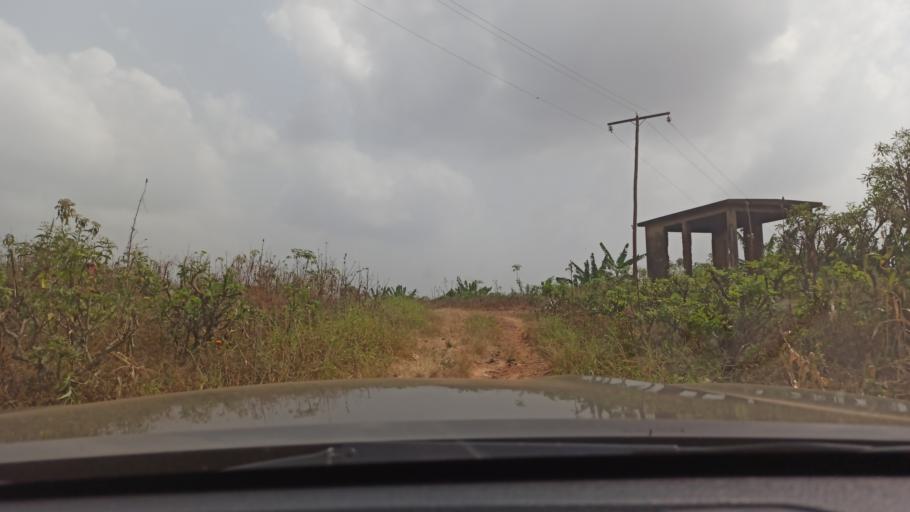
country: CM
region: Centre
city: Yaounde
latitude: 3.8870
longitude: 11.4863
